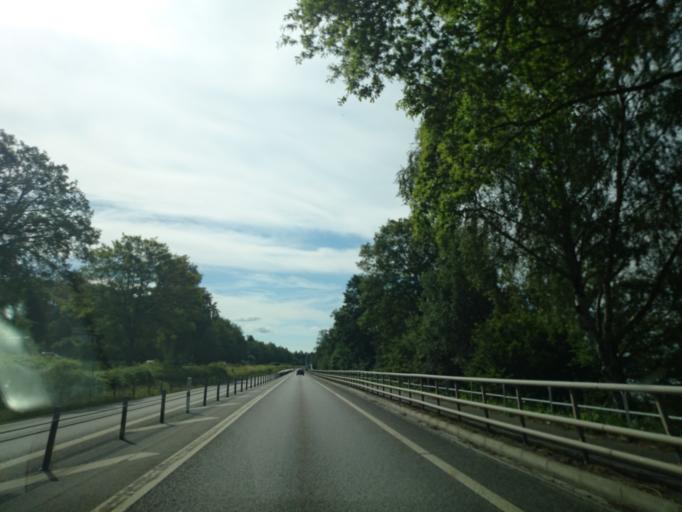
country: SE
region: Kalmar
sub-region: Vasterviks Kommun
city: Vaestervik
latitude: 57.8000
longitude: 16.5130
